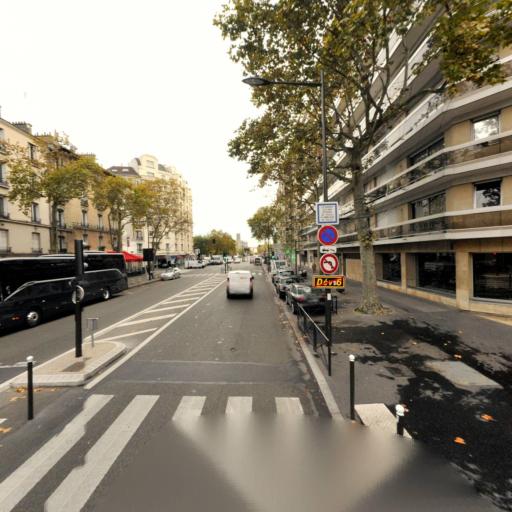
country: FR
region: Ile-de-France
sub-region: Departement des Hauts-de-Seine
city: Boulogne-Billancourt
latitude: 48.8387
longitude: 2.2504
